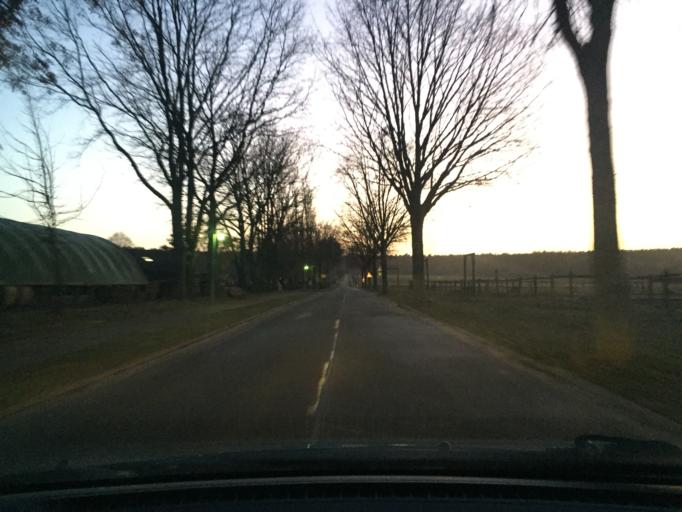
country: DE
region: Lower Saxony
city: Gohrde
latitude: 53.1827
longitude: 10.9268
